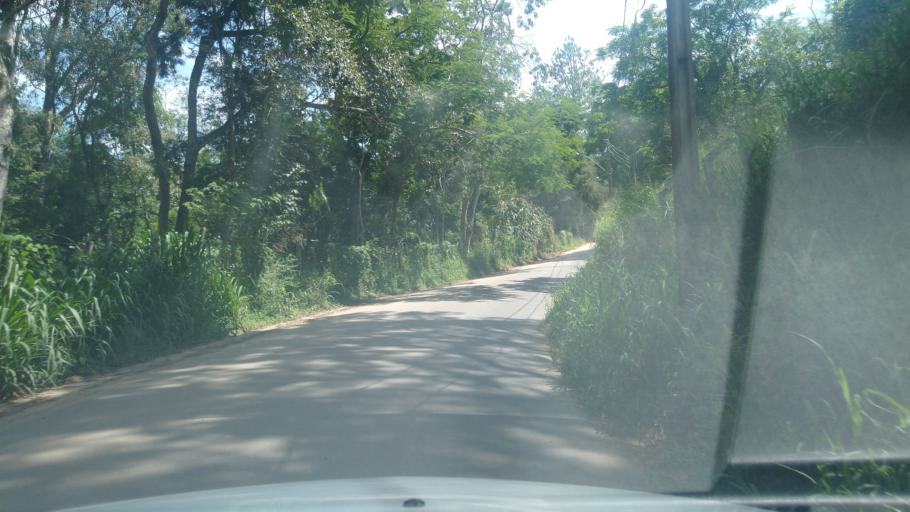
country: BR
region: Minas Gerais
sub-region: Extrema
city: Extrema
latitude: -22.7810
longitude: -46.2872
